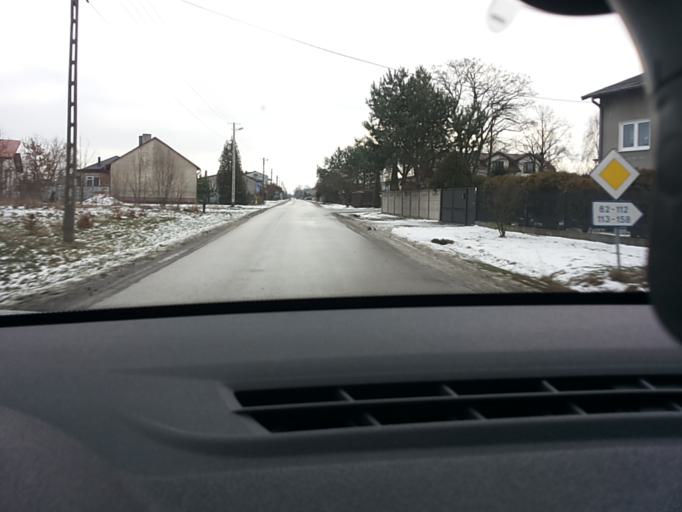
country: PL
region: Lodz Voivodeship
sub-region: Powiat skierniewicki
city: Makow
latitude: 52.0050
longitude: 20.0714
